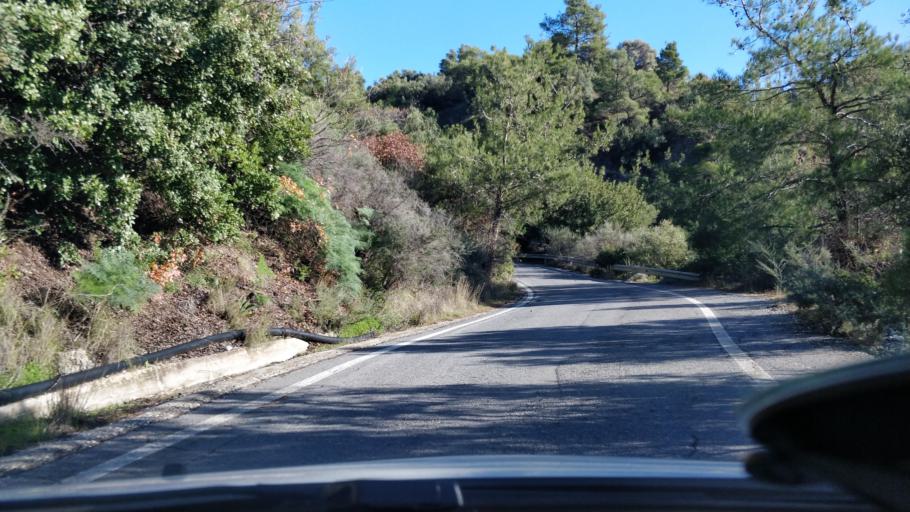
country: GR
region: Crete
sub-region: Nomos Lasithiou
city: Gra Liyia
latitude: 35.0492
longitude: 25.5795
